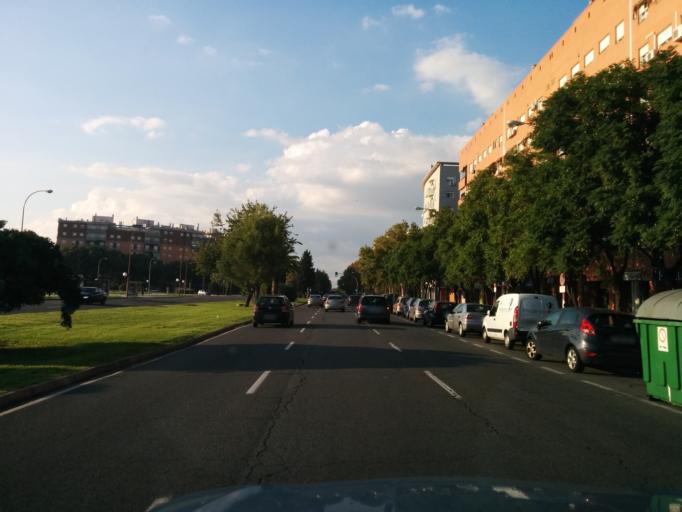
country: ES
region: Andalusia
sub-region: Provincia de Sevilla
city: Sevilla
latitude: 37.3951
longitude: -5.9218
